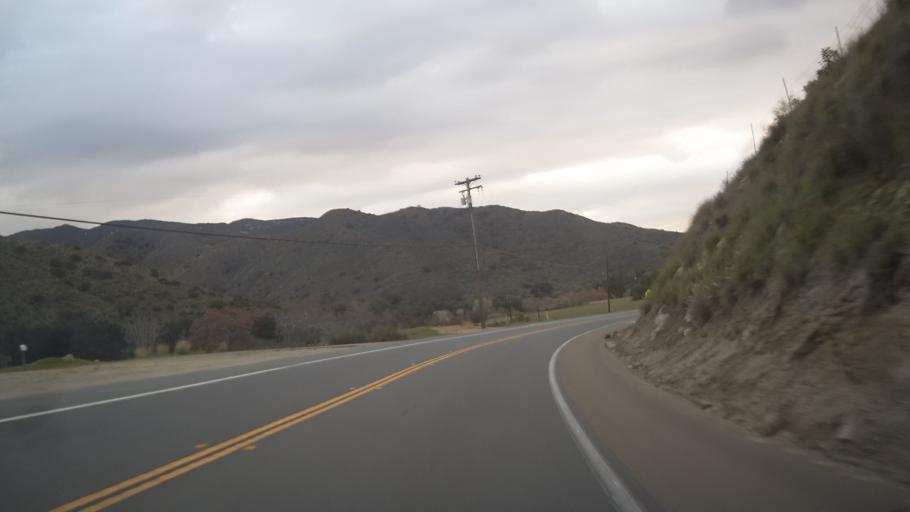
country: US
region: California
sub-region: San Diego County
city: Crest
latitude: 32.7815
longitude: -116.8477
